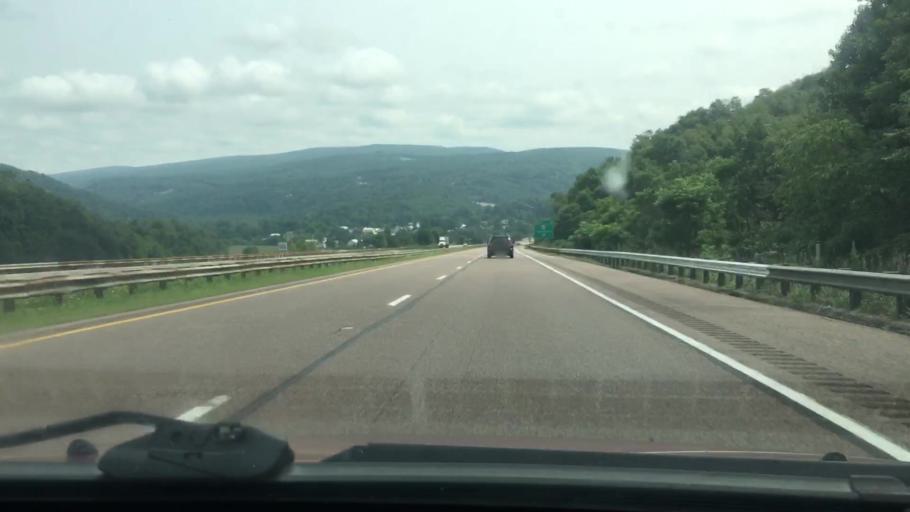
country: US
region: West Virginia
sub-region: Preston County
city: Terra Alta
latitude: 39.6620
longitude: -79.4214
